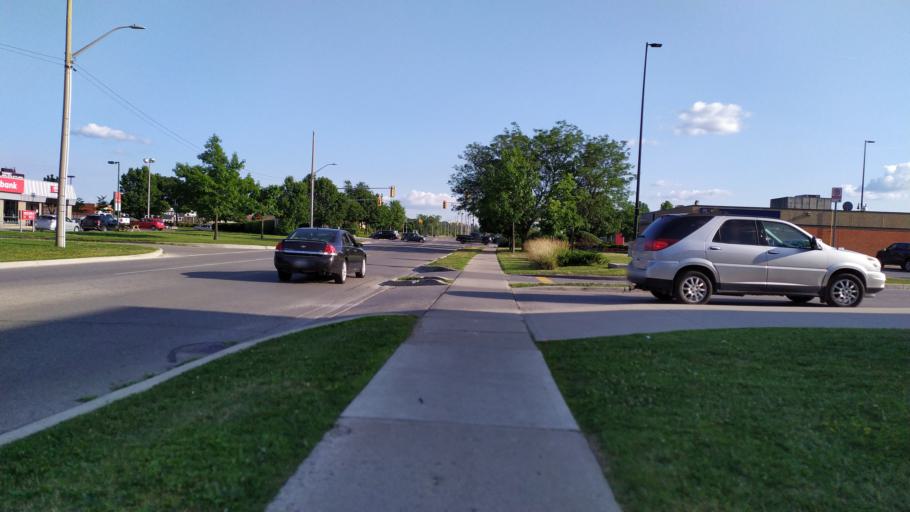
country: CA
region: Ontario
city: Stratford
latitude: 43.3719
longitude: -80.9484
